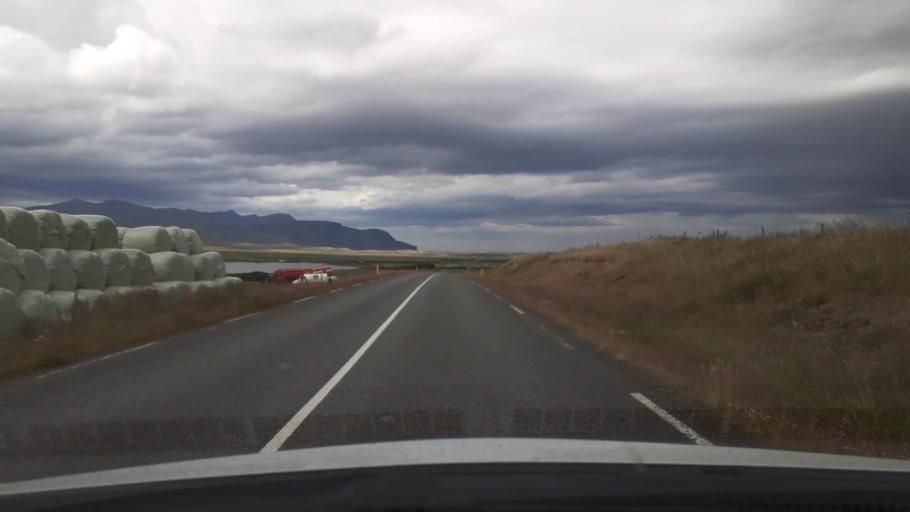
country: IS
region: West
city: Borgarnes
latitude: 64.5438
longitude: -21.5808
